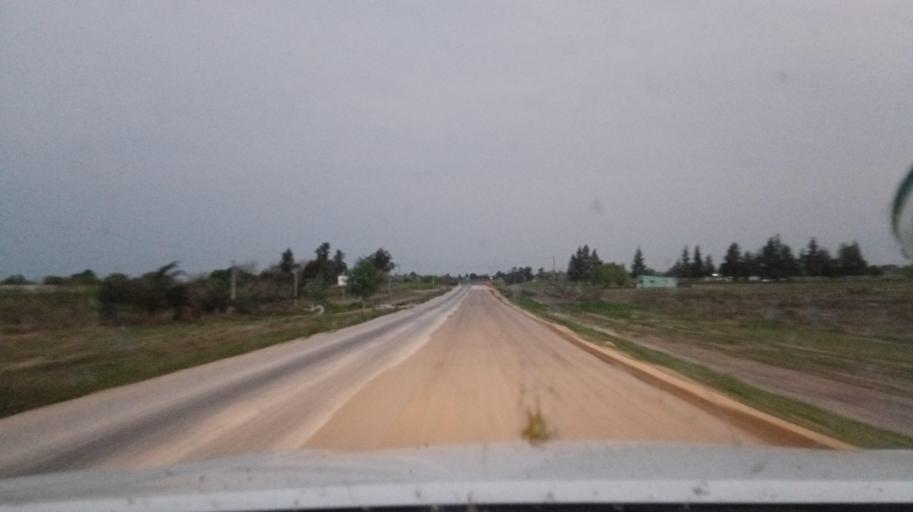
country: UY
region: Canelones
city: Sauce
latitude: -34.5650
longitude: -56.1019
